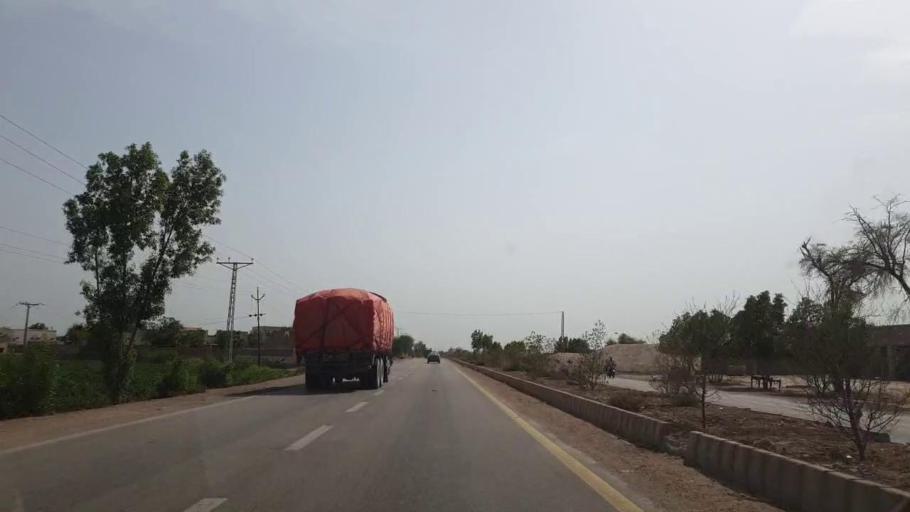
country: PK
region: Sindh
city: Sakrand
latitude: 26.2071
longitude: 68.3204
